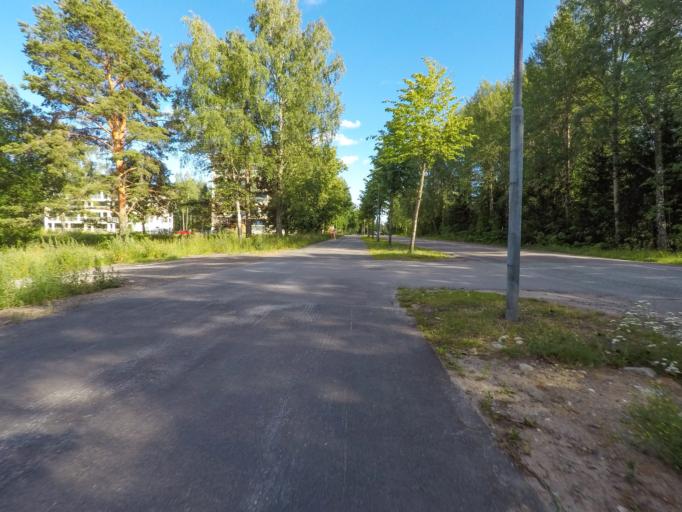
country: FI
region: South Karelia
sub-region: Lappeenranta
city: Lappeenranta
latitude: 61.0708
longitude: 28.1535
